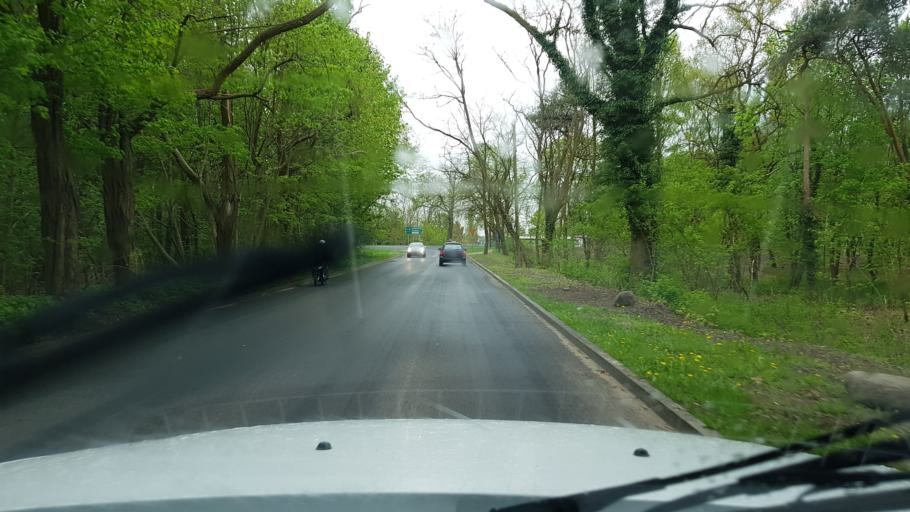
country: PL
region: West Pomeranian Voivodeship
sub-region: Powiat mysliborski
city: Debno
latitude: 52.7431
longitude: 14.7121
